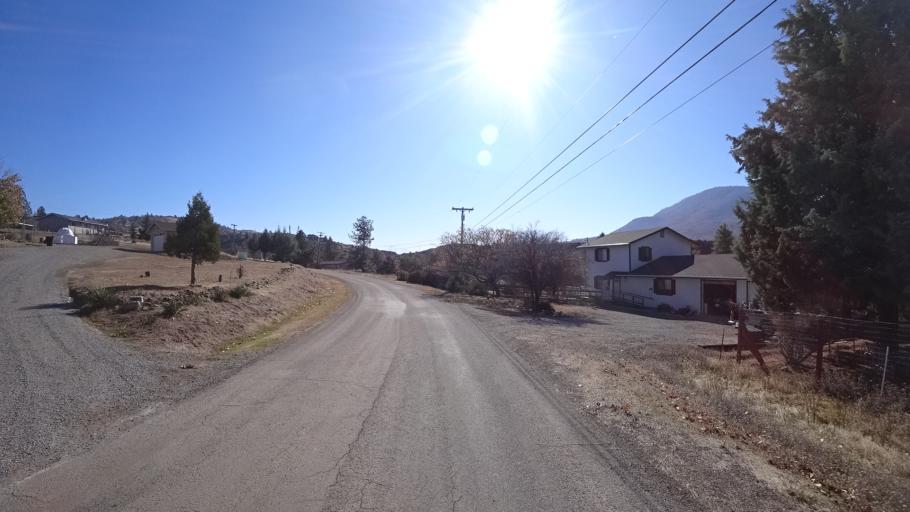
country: US
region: California
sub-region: Siskiyou County
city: Montague
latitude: 41.8990
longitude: -122.4869
